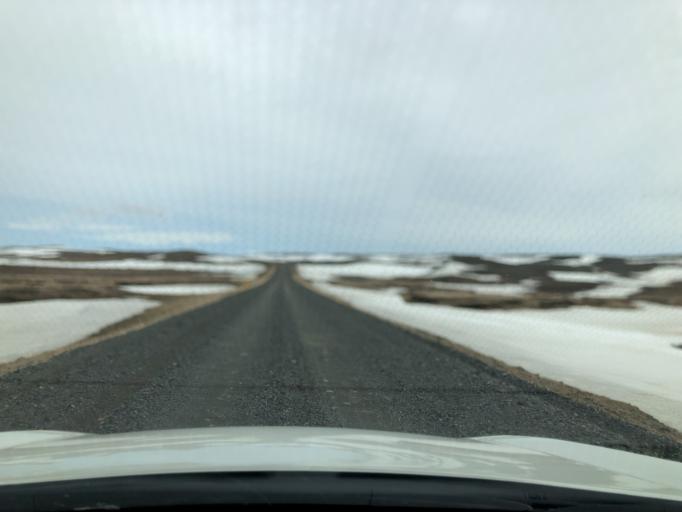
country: IS
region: East
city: Egilsstadir
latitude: 65.3015
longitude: -15.4082
